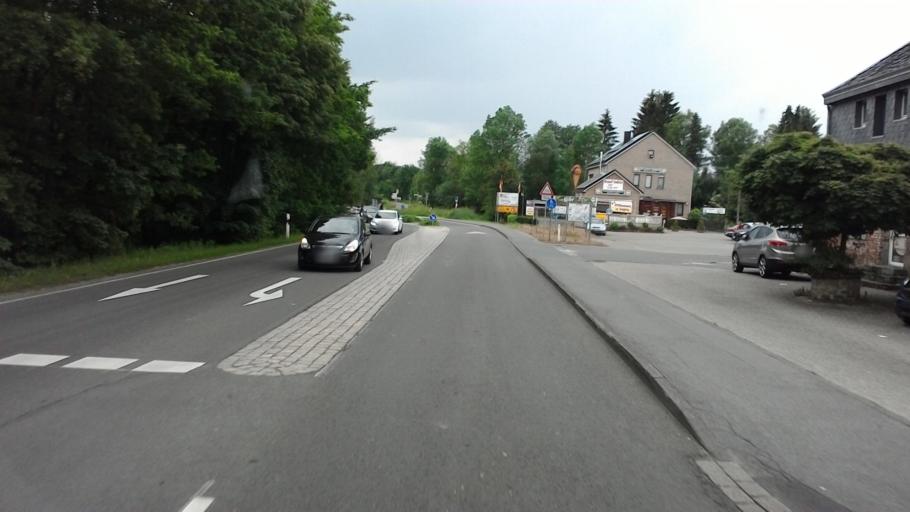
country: DE
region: North Rhine-Westphalia
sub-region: Regierungsbezirk Koln
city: Roetgen
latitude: 50.6486
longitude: 6.1841
